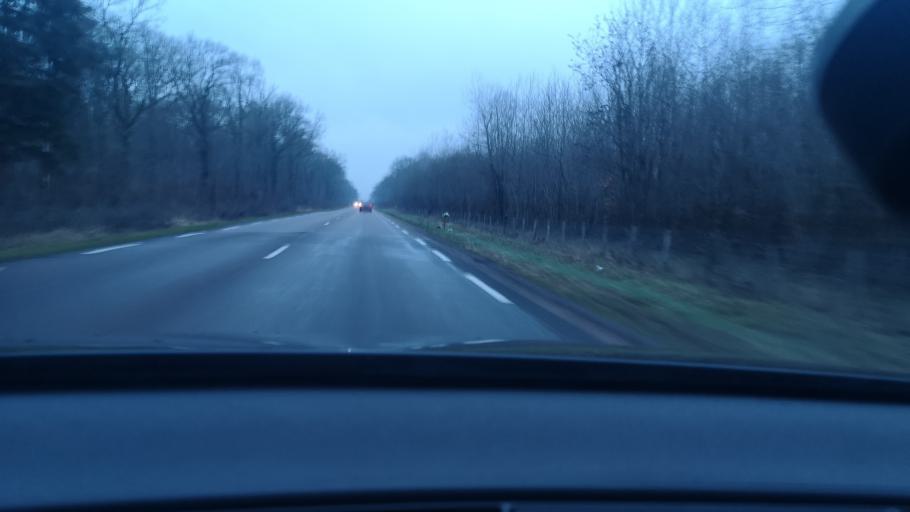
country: FR
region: Bourgogne
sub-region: Departement de la Cote-d'Or
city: Seurre
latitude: 47.0052
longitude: 5.0444
